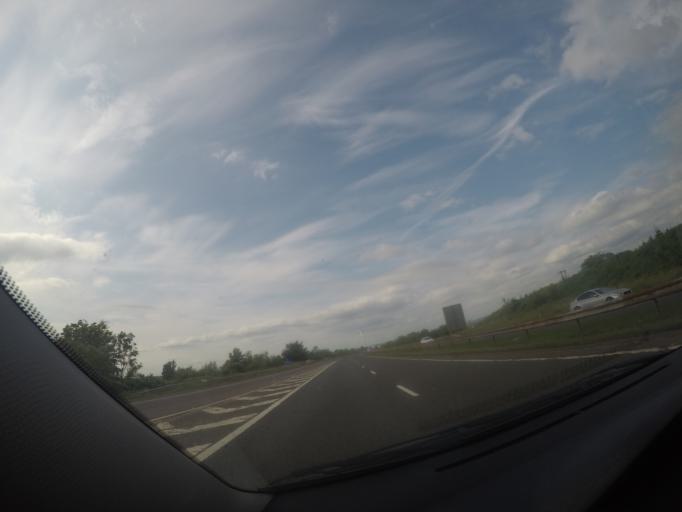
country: GB
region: Scotland
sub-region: South Lanarkshire
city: Larkhall
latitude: 55.7153
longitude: -3.9561
